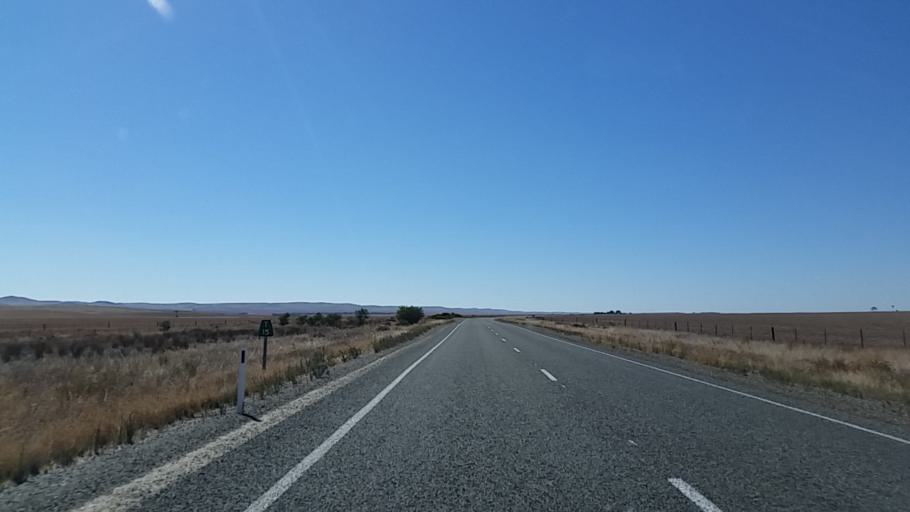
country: AU
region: South Australia
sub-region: Northern Areas
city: Jamestown
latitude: -33.2727
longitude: 138.8683
